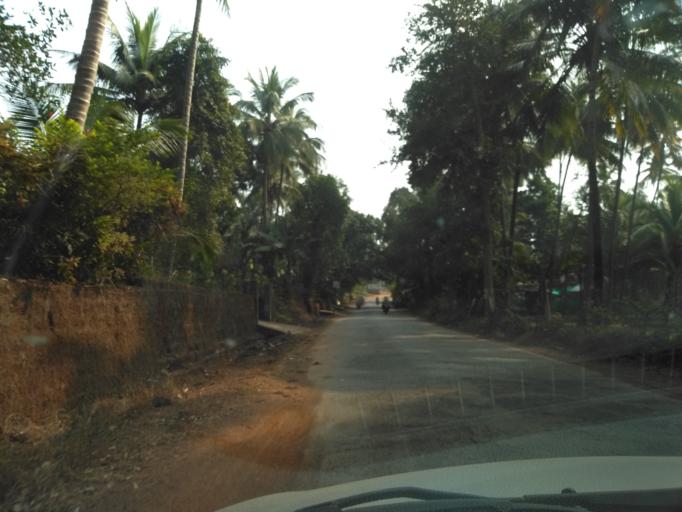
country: IN
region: Maharashtra
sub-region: Sindhudurg
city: Savantvadi
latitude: 15.8185
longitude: 73.8985
